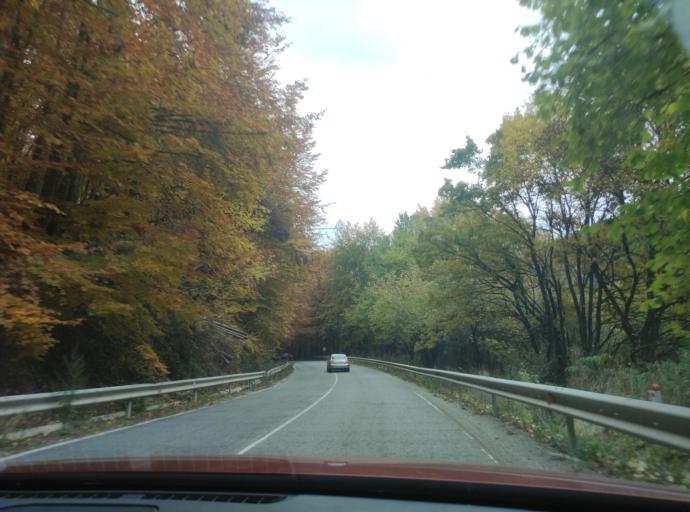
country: BG
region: Sofiya
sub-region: Obshtina Godech
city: Godech
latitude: 43.0242
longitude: 23.1372
